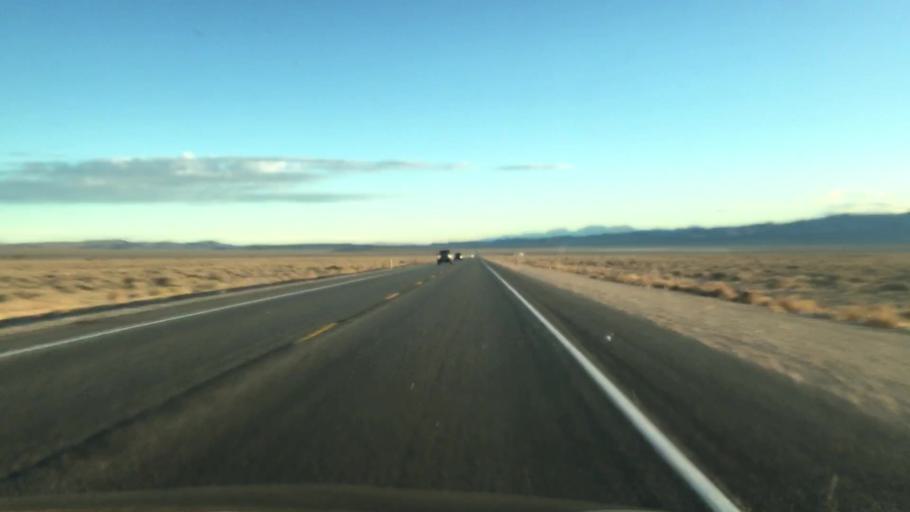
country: US
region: Nevada
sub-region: Esmeralda County
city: Goldfield
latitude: 37.5195
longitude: -117.1894
